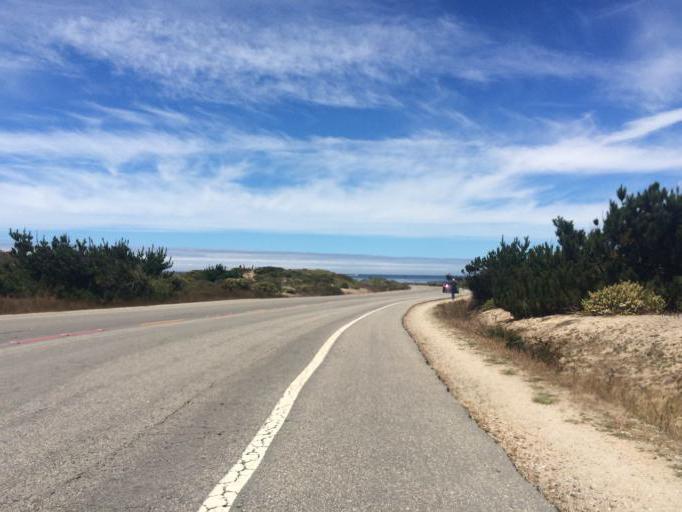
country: US
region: California
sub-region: Monterey County
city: Del Monte Forest
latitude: 36.6084
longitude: -121.9471
